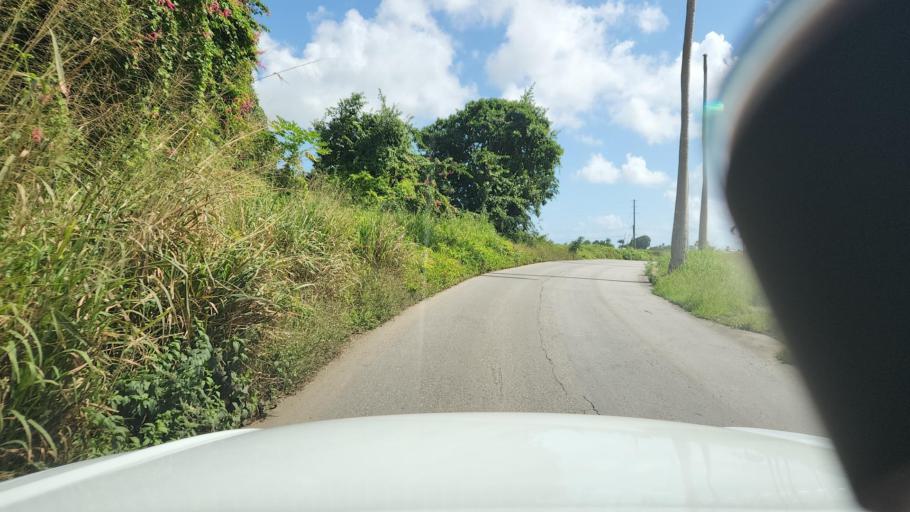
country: BB
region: Saint John
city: Four Cross Roads
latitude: 13.1694
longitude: -59.4859
